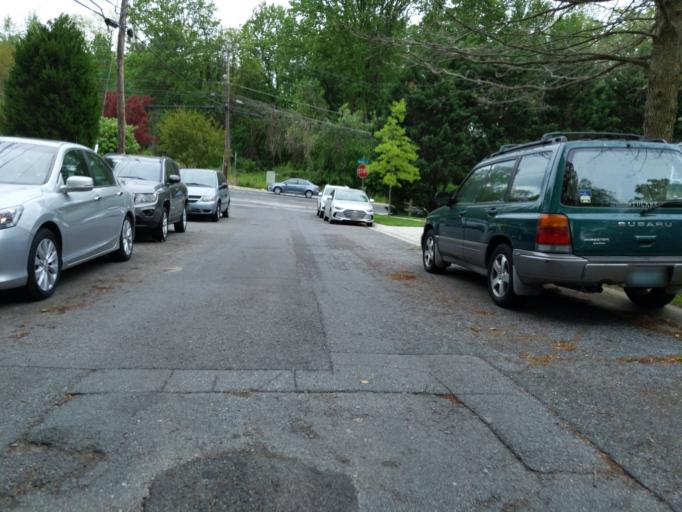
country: US
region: Maryland
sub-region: Montgomery County
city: Forest Glen
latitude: 39.0269
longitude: -77.0376
